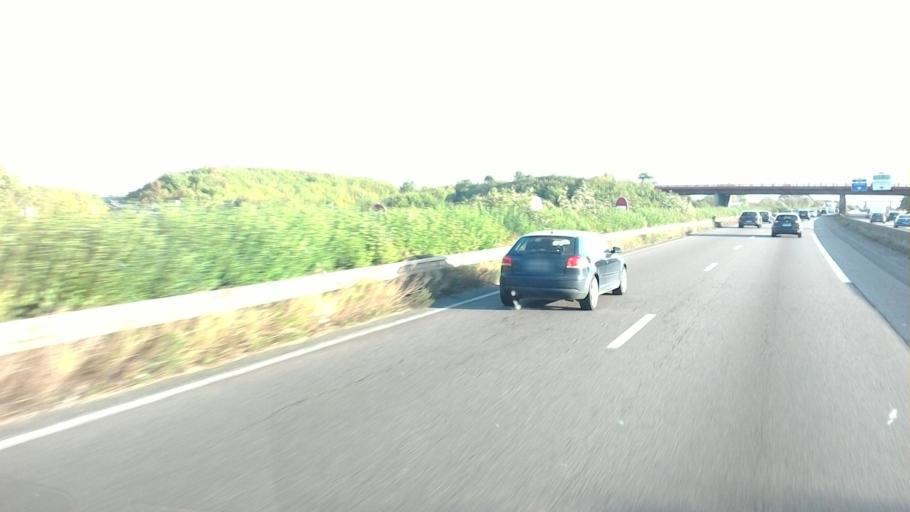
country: FR
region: Lorraine
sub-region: Departement de la Moselle
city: Illange
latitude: 49.3352
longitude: 6.1849
